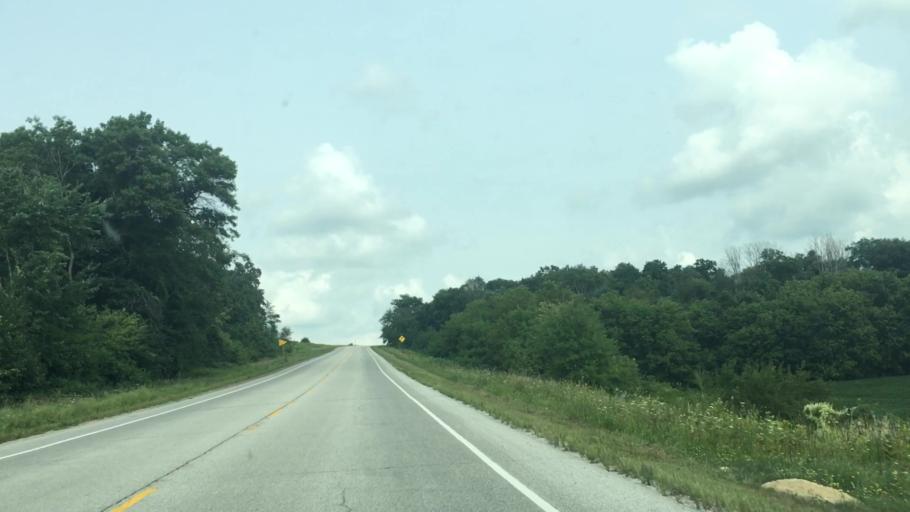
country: US
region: Minnesota
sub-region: Fillmore County
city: Harmony
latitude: 43.6374
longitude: -91.9299
